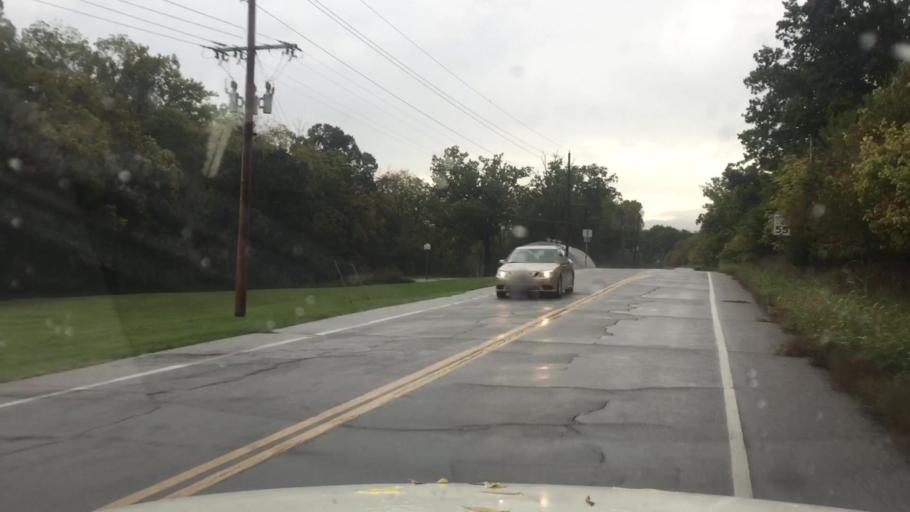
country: US
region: Missouri
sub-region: Boone County
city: Columbia
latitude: 38.8811
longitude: -92.4215
